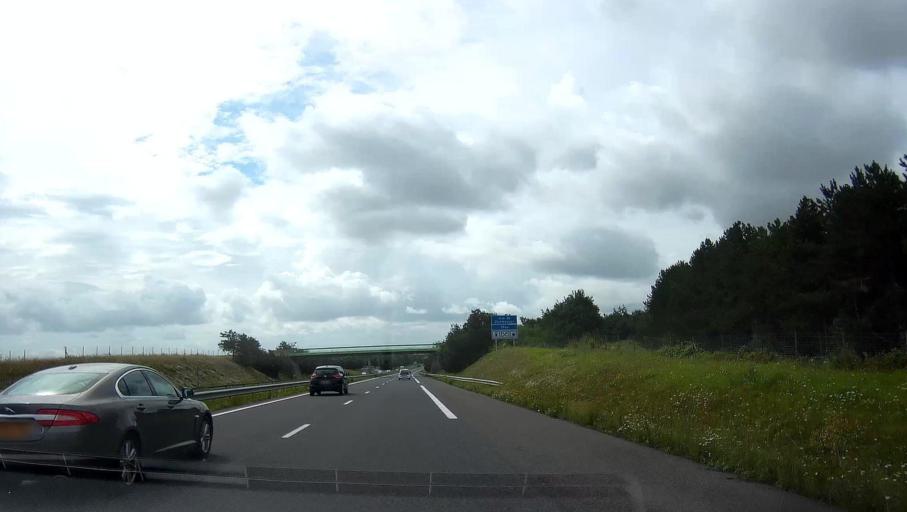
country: FR
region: Champagne-Ardenne
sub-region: Departement de la Marne
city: Compertrix
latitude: 48.8917
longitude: 4.2881
